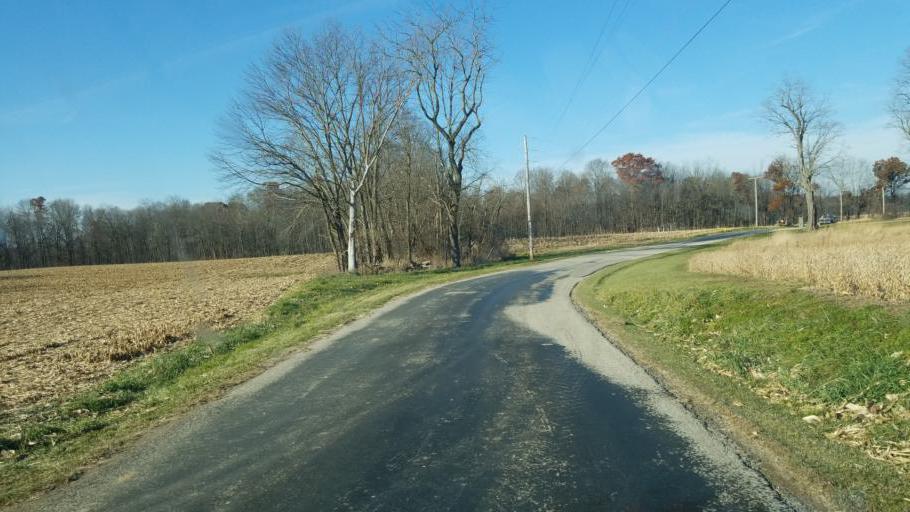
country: US
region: Ohio
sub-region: Richland County
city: Lincoln Heights
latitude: 40.8512
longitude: -82.4720
